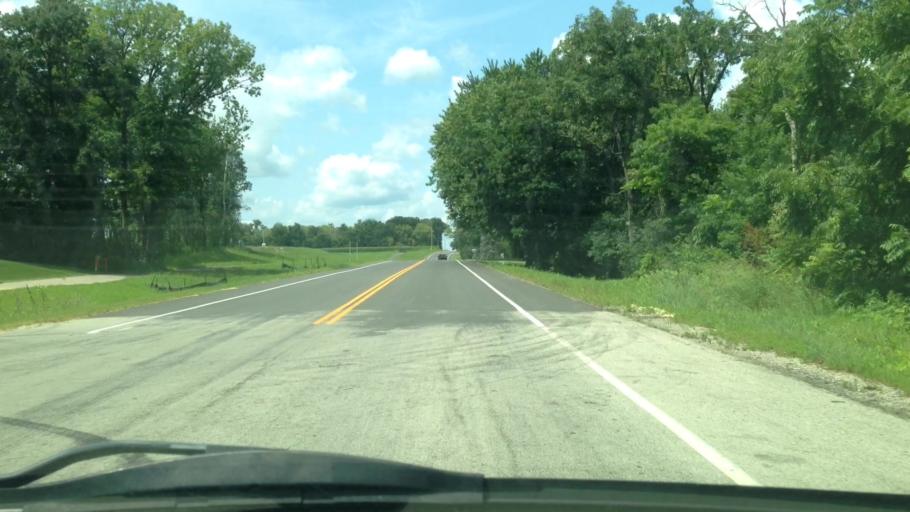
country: US
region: Minnesota
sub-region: Olmsted County
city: Rochester
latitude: 43.9531
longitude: -92.4974
